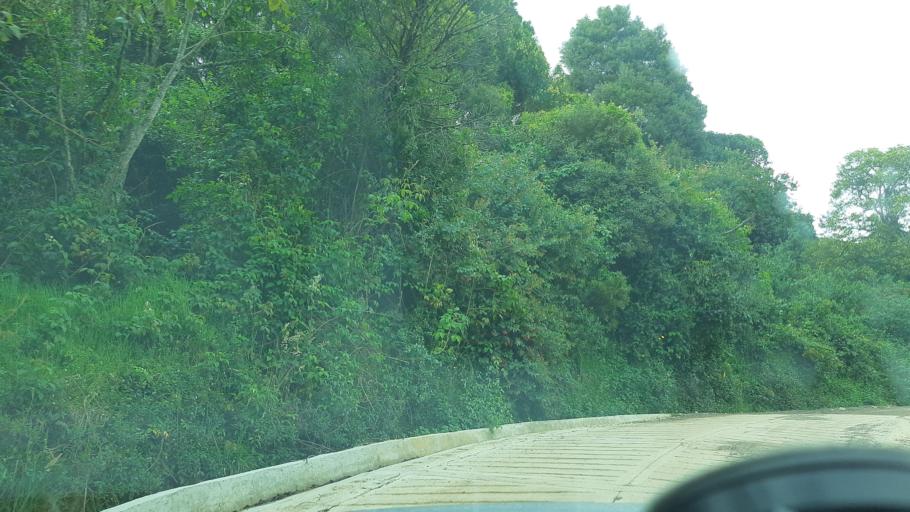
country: CO
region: Boyaca
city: Cucaita
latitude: 5.5067
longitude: -73.4342
